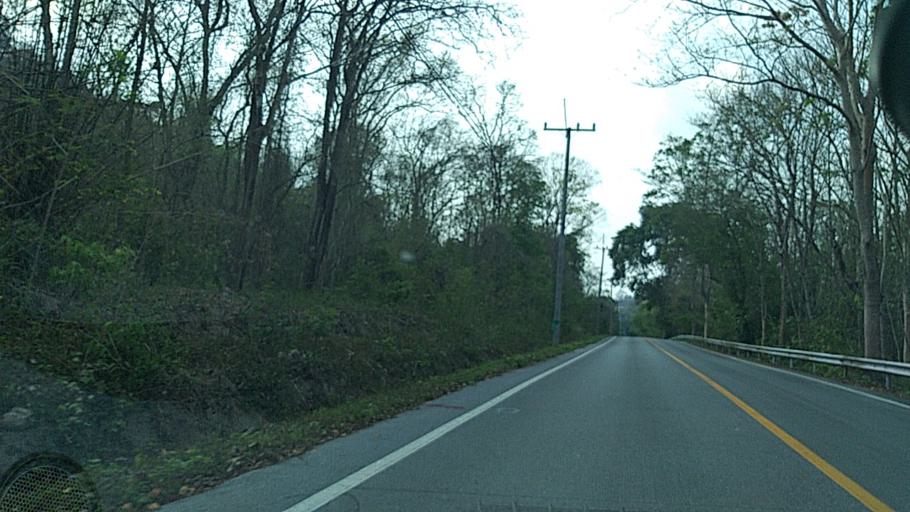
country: TH
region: Sara Buri
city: Saraburi
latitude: 14.4502
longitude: 100.9542
